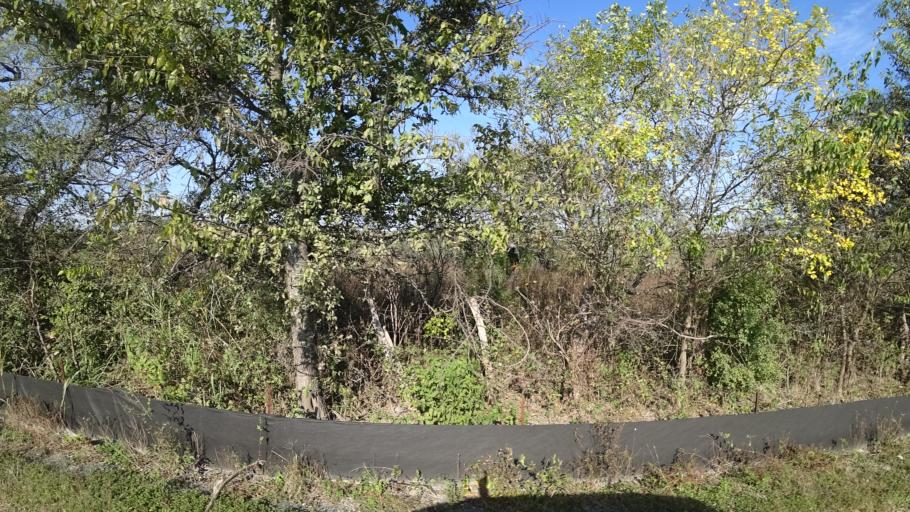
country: US
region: Texas
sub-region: Travis County
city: Pflugerville
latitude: 30.4026
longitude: -97.6219
